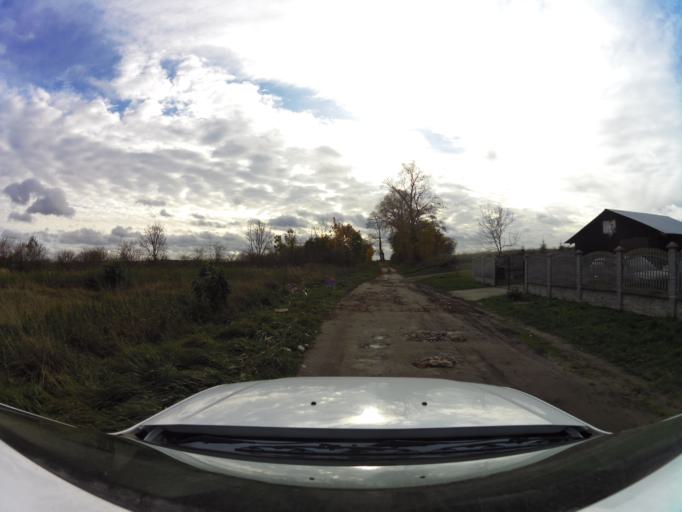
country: PL
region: West Pomeranian Voivodeship
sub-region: Powiat gryficki
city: Gryfice
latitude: 53.8880
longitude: 15.1203
